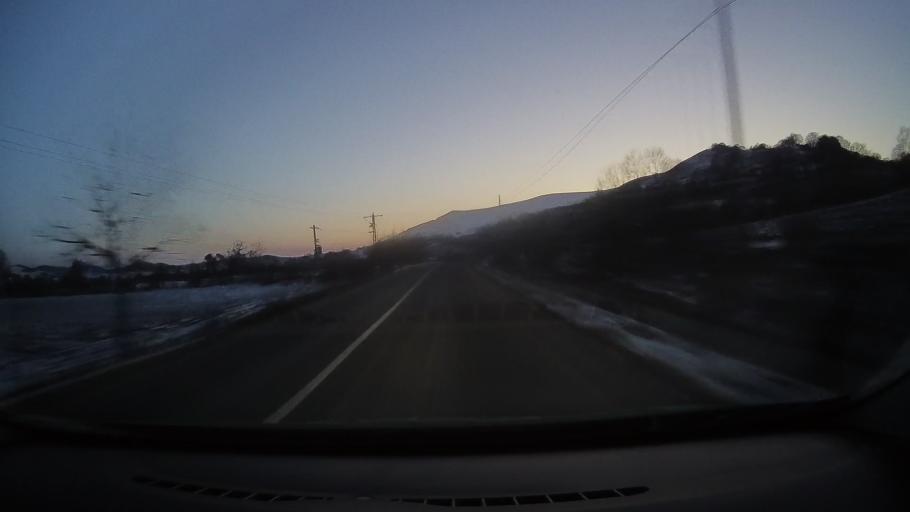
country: RO
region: Sibiu
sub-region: Comuna Alma
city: Alma
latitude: 46.2010
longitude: 24.4481
